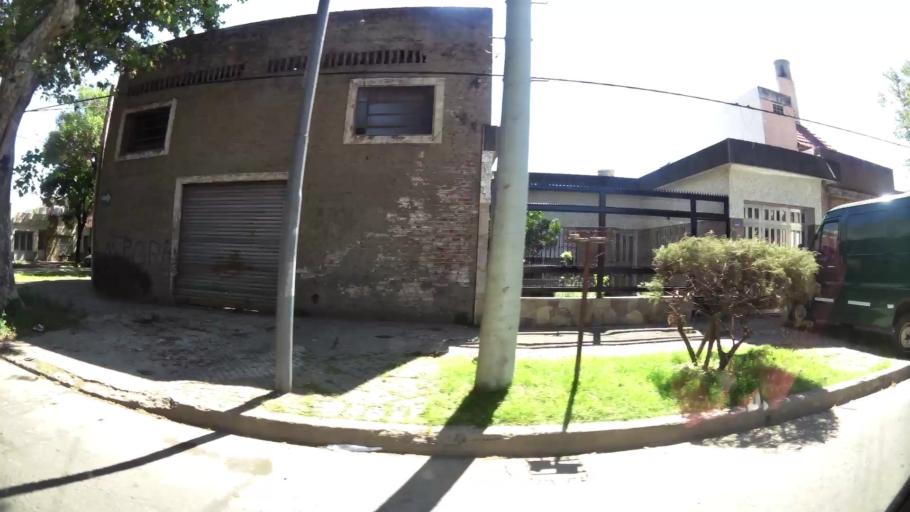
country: AR
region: Santa Fe
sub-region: Departamento de Rosario
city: Rosario
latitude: -32.9375
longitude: -60.6936
